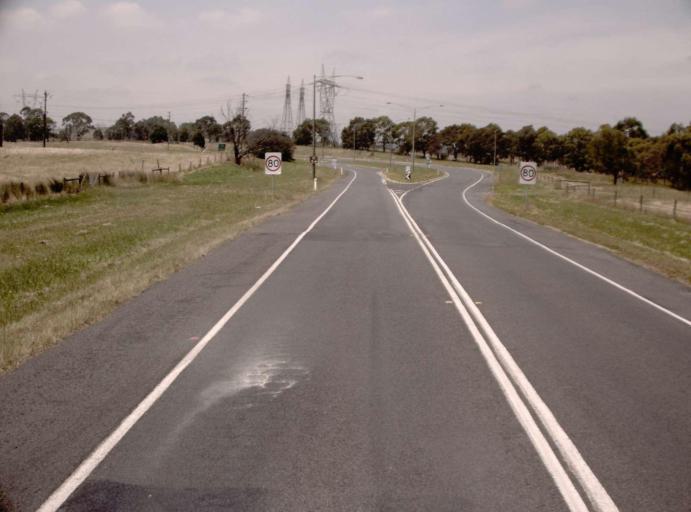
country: AU
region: Victoria
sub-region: Latrobe
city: Traralgon
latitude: -38.2465
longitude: 146.5472
